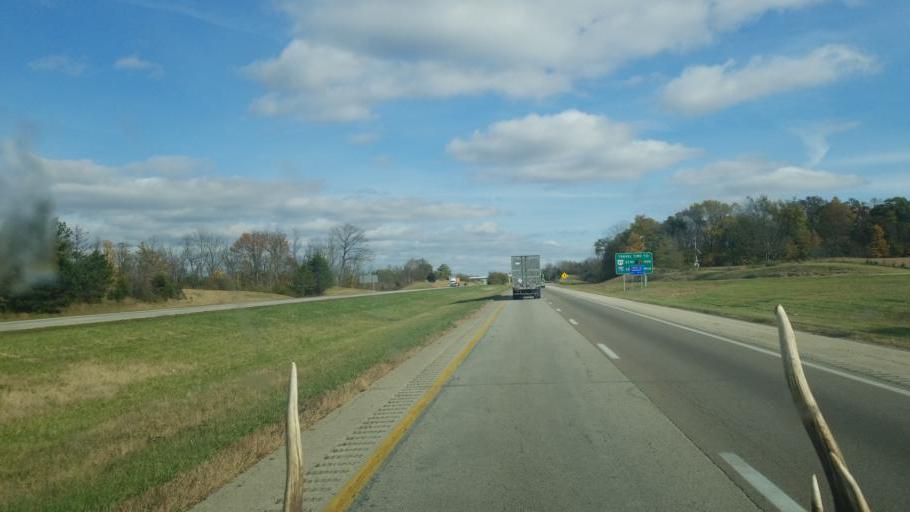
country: US
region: Ohio
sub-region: Preble County
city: New Paris
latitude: 39.8285
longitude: -84.8020
